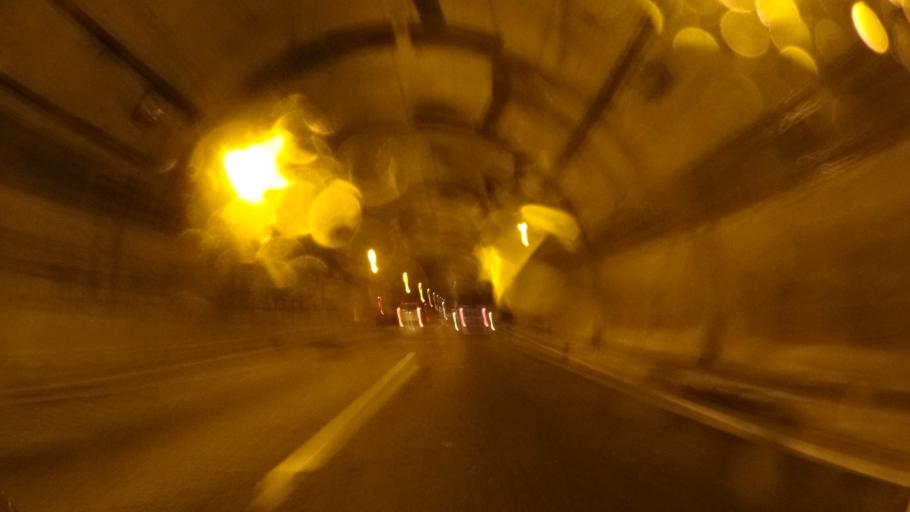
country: JP
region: Kagoshima
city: Okuchi-shinohara
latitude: 31.9677
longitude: 130.7469
